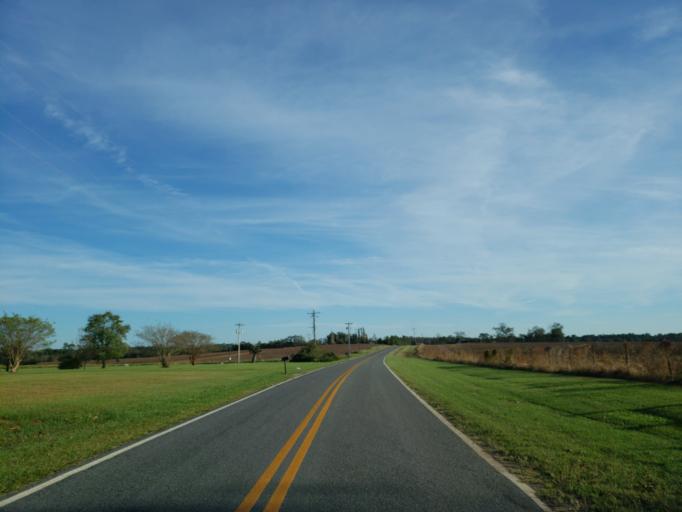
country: US
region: Georgia
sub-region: Dooly County
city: Vienna
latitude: 32.0424
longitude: -83.7545
